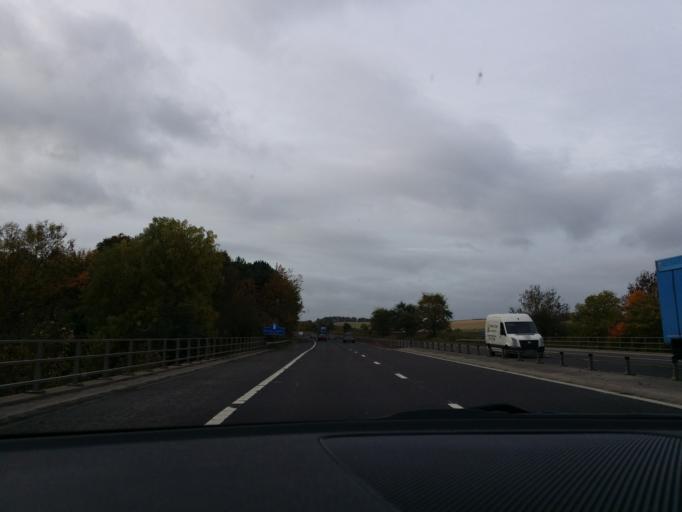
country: GB
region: Scotland
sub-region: West Lothian
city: Linlithgow
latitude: 55.9830
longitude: -3.6278
